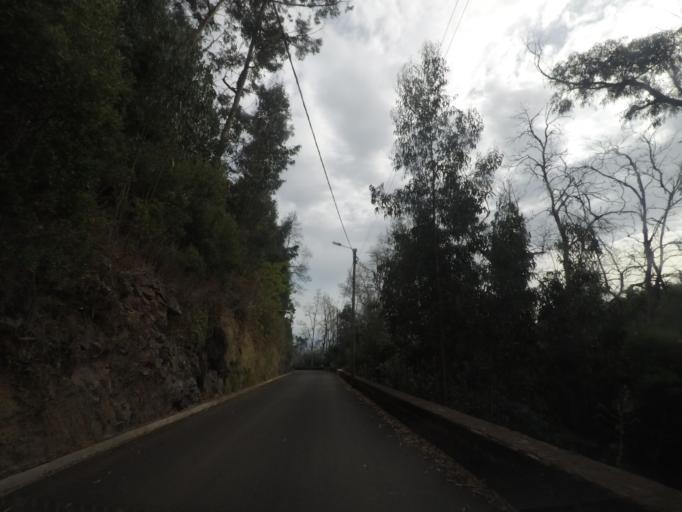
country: PT
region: Madeira
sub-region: Calheta
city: Arco da Calheta
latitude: 32.7420
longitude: -17.1531
